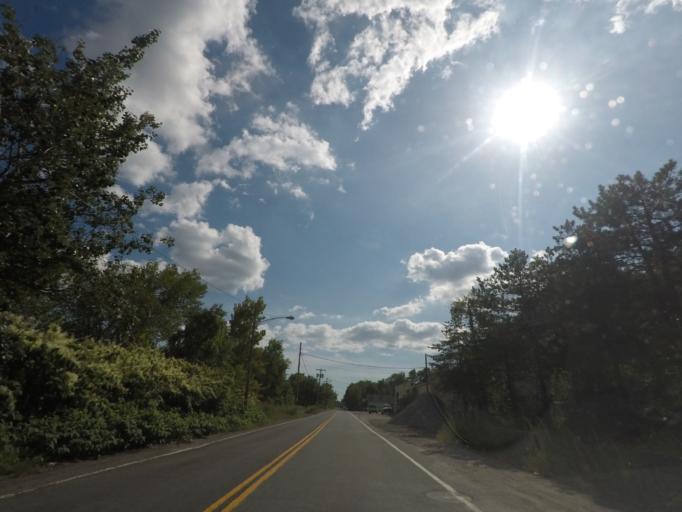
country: US
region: New York
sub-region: Albany County
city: Watervliet
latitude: 42.7184
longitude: -73.7171
